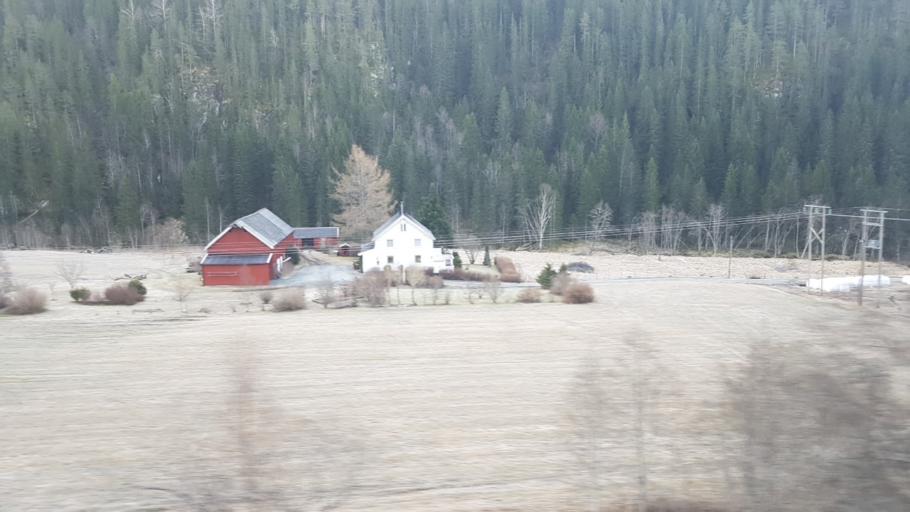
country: NO
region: Nord-Trondelag
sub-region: Stjordal
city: Stjordalshalsen
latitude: 63.5990
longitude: 11.0234
